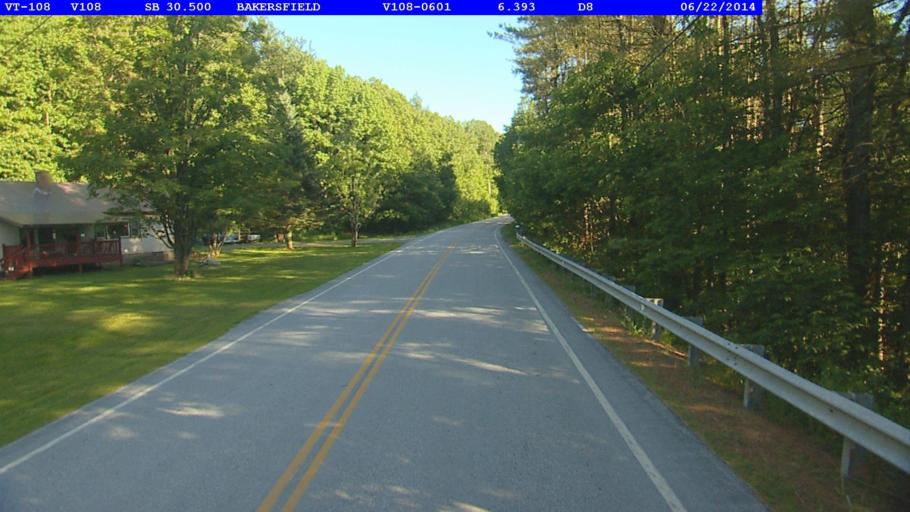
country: US
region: Vermont
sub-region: Franklin County
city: Enosburg Falls
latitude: 44.8183
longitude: -72.7911
